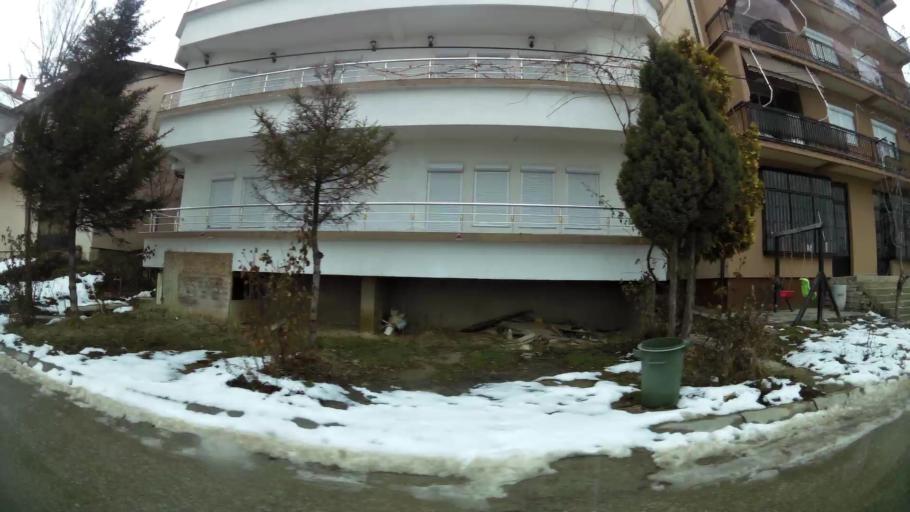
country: XK
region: Pristina
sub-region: Komuna e Prishtines
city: Pristina
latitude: 42.6751
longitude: 21.1847
